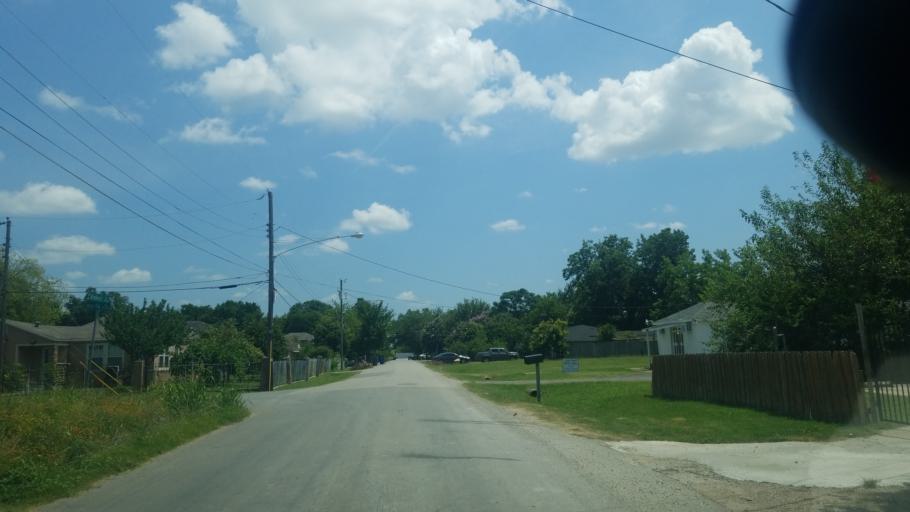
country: US
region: Texas
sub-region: Dallas County
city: Dallas
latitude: 32.7186
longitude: -96.7651
